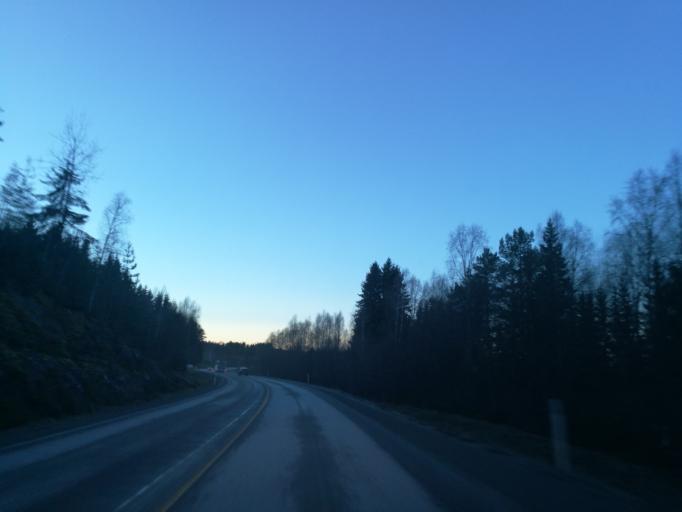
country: NO
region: Hedmark
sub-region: Eidskog
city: Skotterud
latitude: 59.9737
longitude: 12.1347
